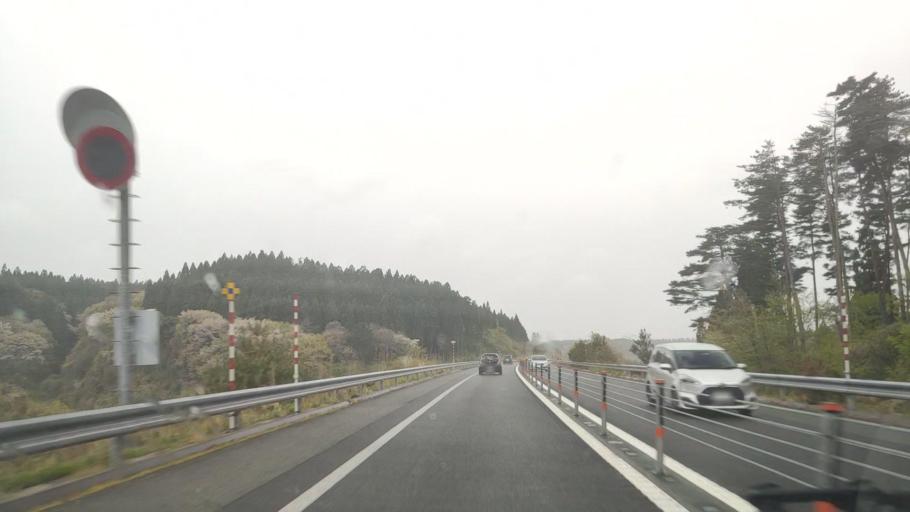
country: JP
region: Akita
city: Noshiromachi
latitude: 40.1941
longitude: 140.1185
